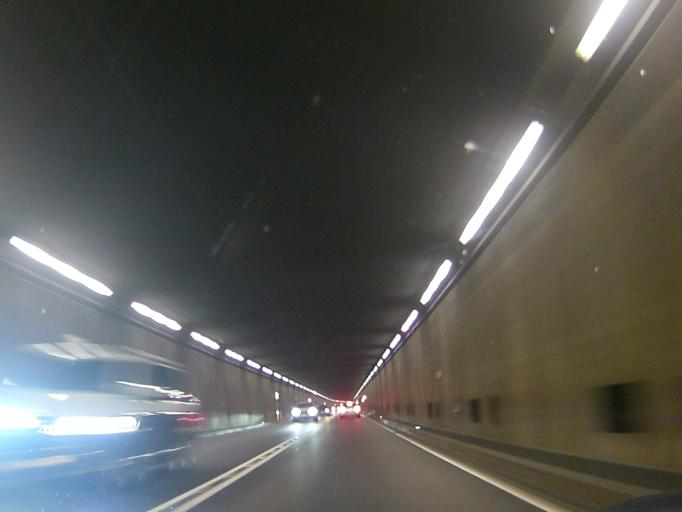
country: CH
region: Uri
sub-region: Uri
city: Andermatt
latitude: 46.5877
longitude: 8.5662
